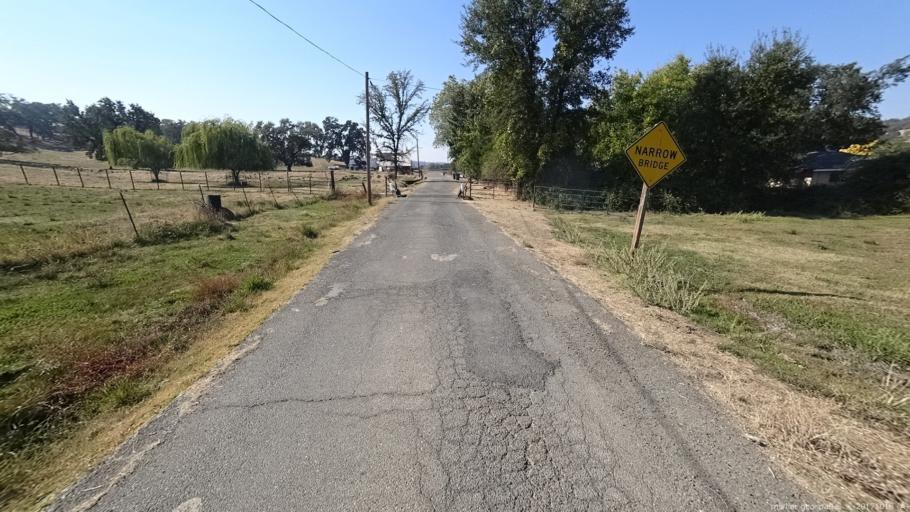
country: US
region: California
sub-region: Shasta County
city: Shingletown
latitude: 40.5549
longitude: -122.0546
